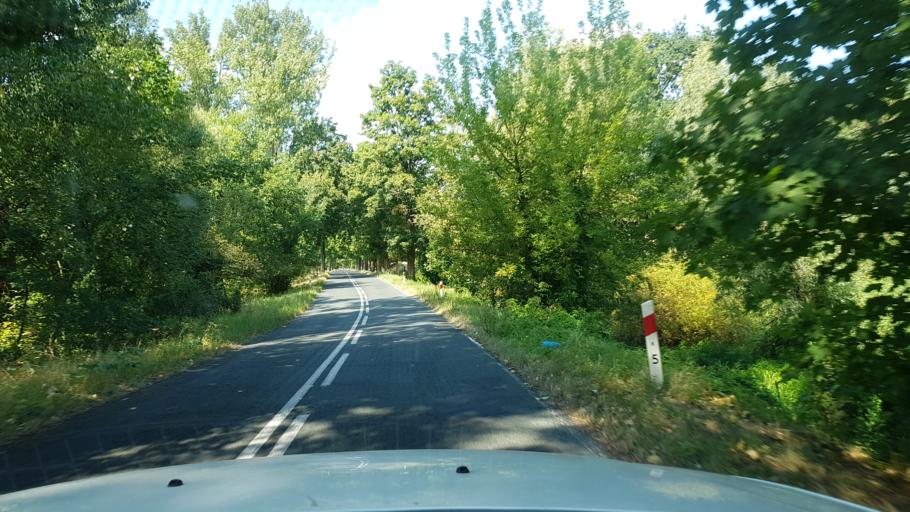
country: PL
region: West Pomeranian Voivodeship
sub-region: Powiat gryfinski
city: Cedynia
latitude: 52.8242
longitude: 14.2265
